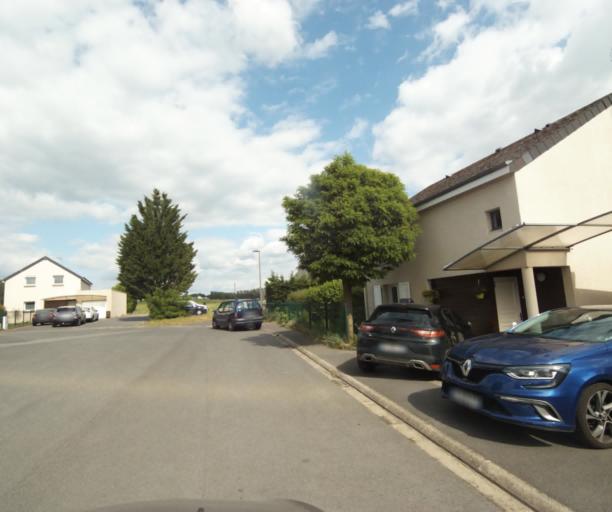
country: FR
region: Champagne-Ardenne
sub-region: Departement des Ardennes
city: Montcy-Notre-Dame
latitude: 49.7608
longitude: 4.7520
